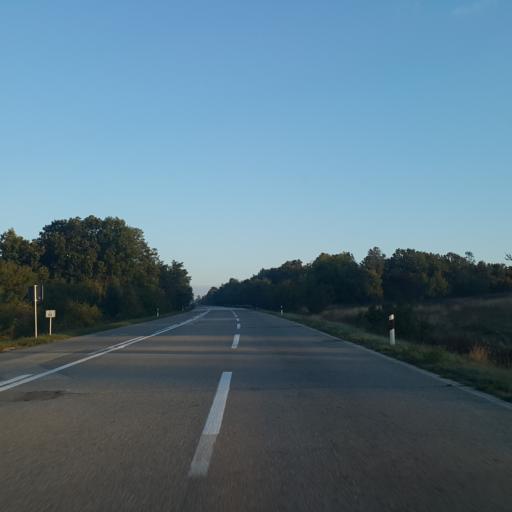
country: RS
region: Central Serbia
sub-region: Borski Okrug
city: Negotin
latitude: 44.1083
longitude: 22.3461
